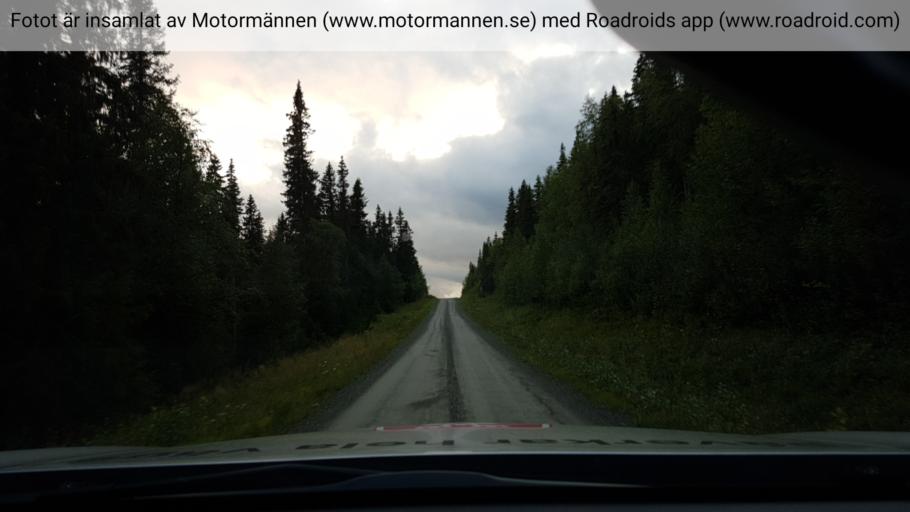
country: SE
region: Vaesterbotten
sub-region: Vilhelmina Kommun
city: Sjoberg
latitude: 65.4950
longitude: 15.5182
